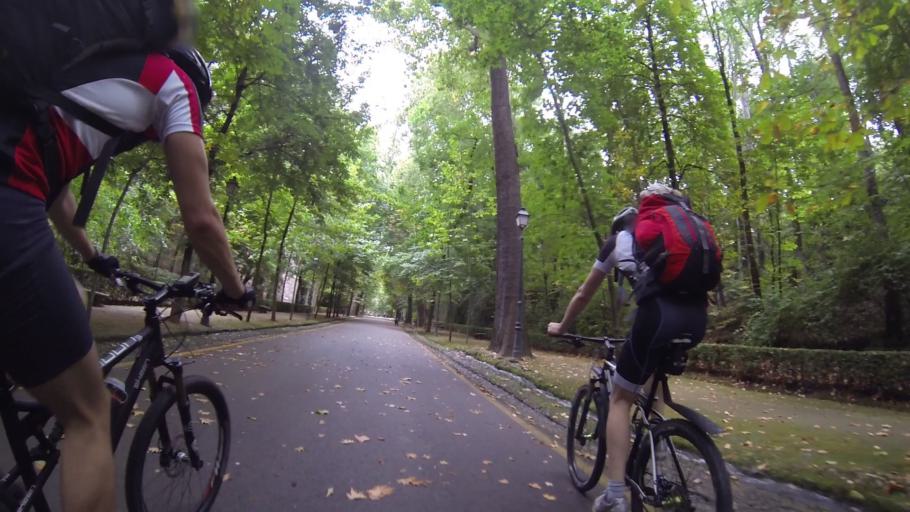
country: ES
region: Andalusia
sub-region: Provincia de Granada
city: Granada
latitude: 37.1757
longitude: -3.5902
